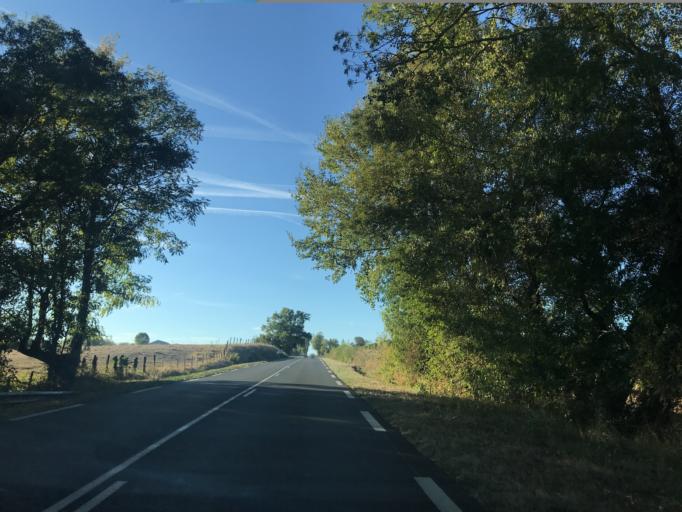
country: FR
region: Poitou-Charentes
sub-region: Departement de la Charente-Maritime
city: Montguyon
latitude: 45.1747
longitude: -0.1112
